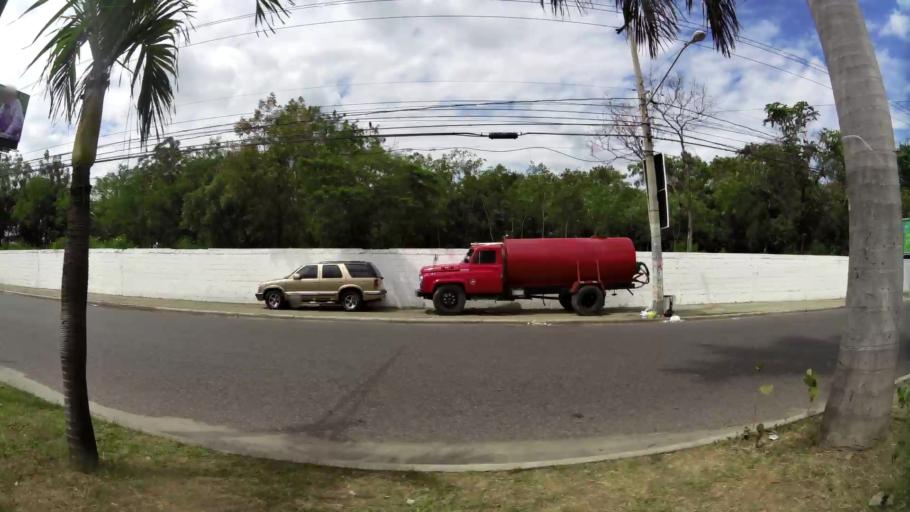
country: DO
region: Santiago
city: Santiago de los Caballeros
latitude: 19.4696
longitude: -70.7130
